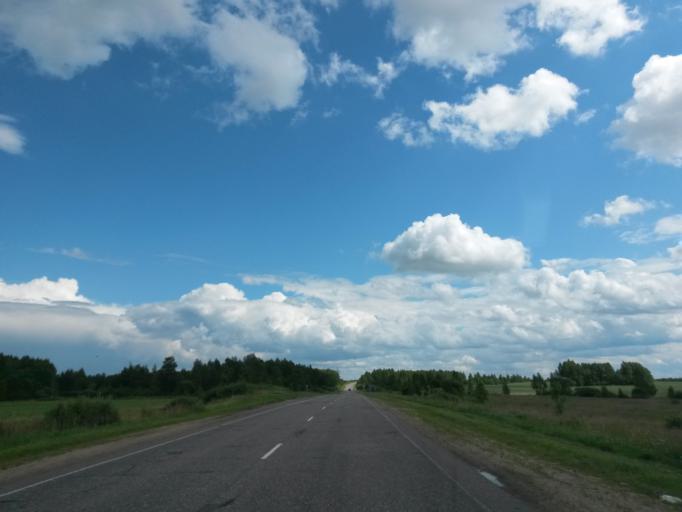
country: RU
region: Ivanovo
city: Pistsovo
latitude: 57.1885
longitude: 40.4378
